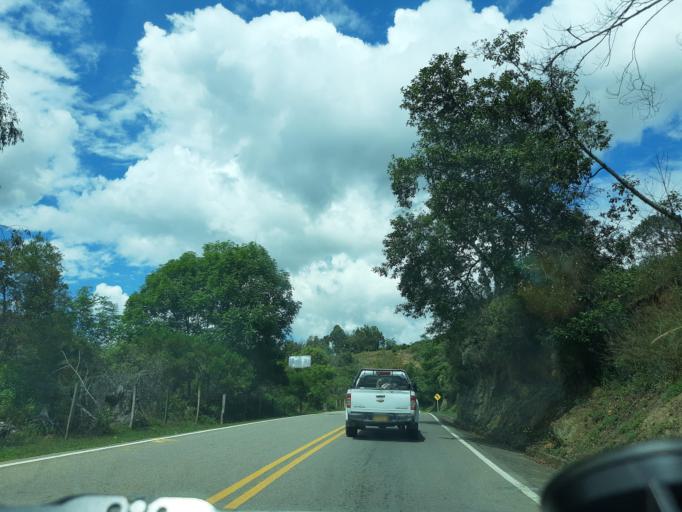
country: CO
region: Boyaca
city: Raquira
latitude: 5.5732
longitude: -73.6830
